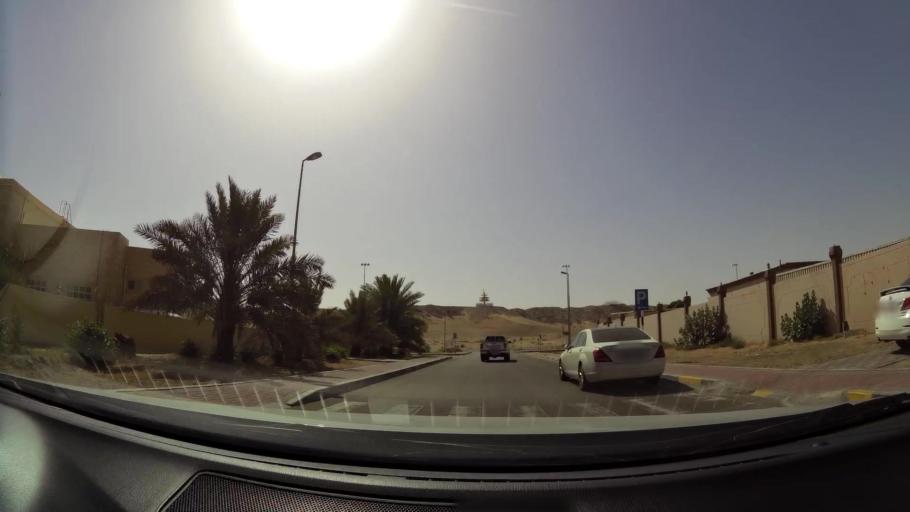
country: OM
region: Al Buraimi
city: Al Buraymi
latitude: 24.3183
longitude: 55.8125
